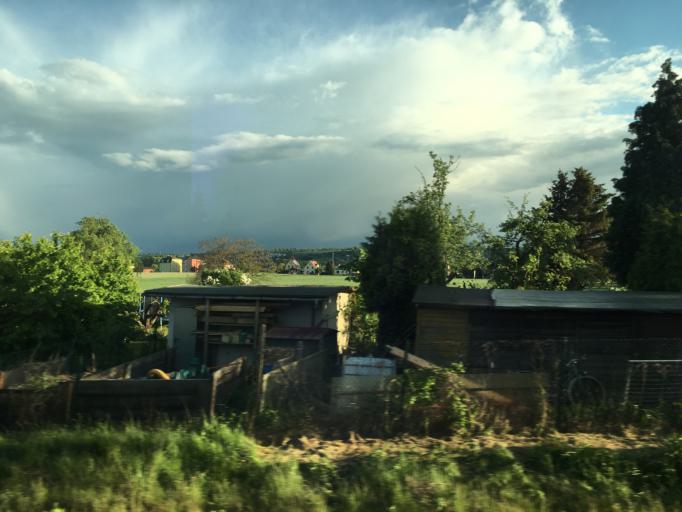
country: DE
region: Saxony
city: Radebeul
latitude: 51.1043
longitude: 13.6457
